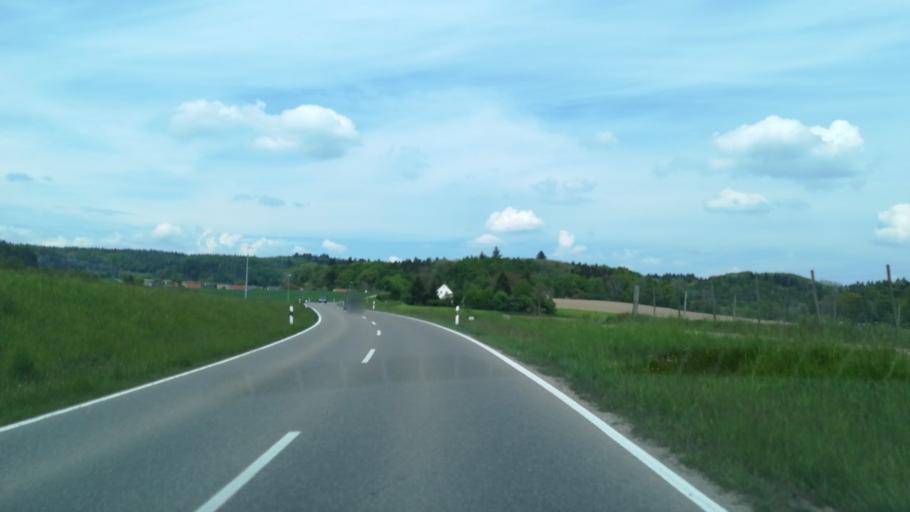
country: DE
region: Baden-Wuerttemberg
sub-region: Freiburg Region
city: Stockach
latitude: 47.8616
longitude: 9.0209
